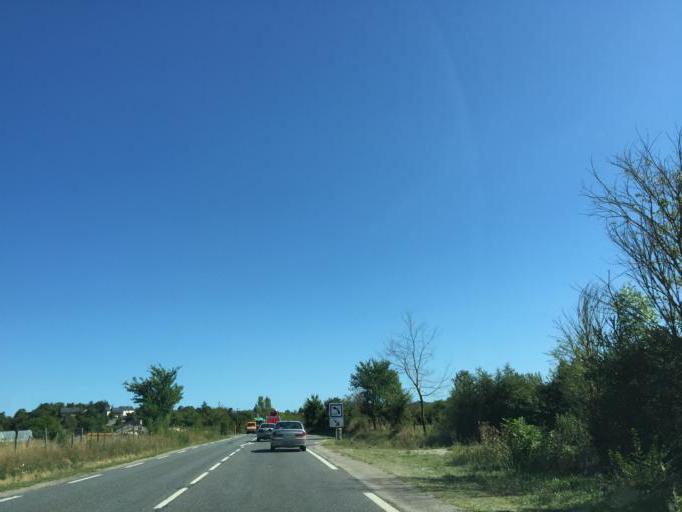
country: FR
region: Midi-Pyrenees
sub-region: Departement de l'Aveyron
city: Severac-le-Chateau
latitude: 44.3411
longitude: 3.0247
